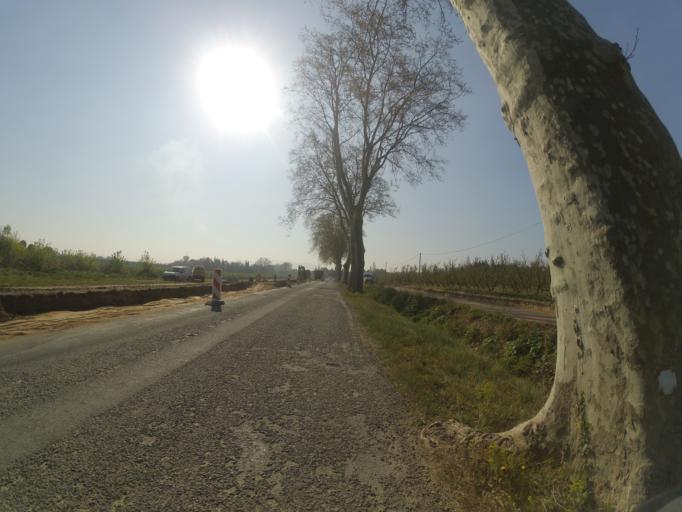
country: FR
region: Languedoc-Roussillon
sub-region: Departement des Pyrenees-Orientales
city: Thuir
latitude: 42.6472
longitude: 2.7369
